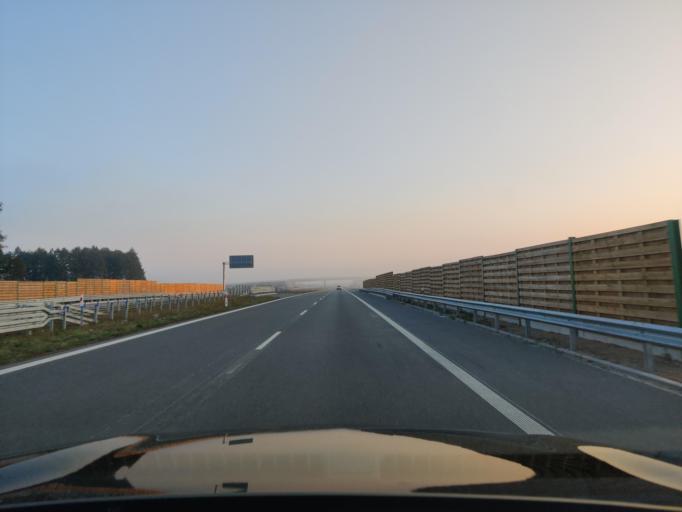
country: PL
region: Masovian Voivodeship
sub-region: Powiat mlawski
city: Strzegowo
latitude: 52.9374
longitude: 20.2917
